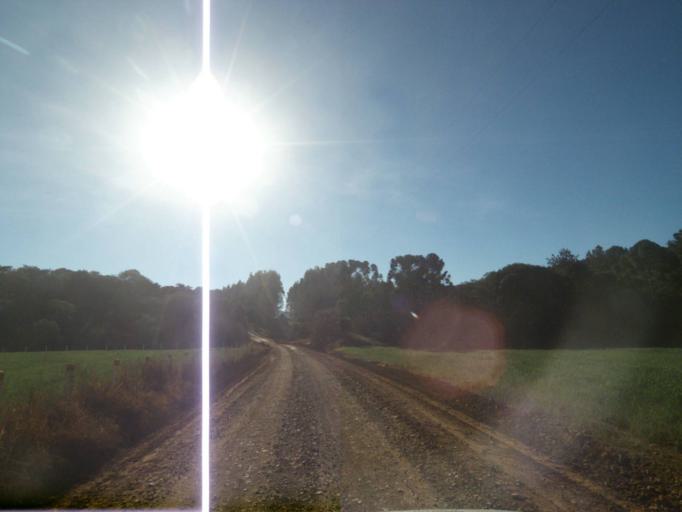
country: BR
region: Parana
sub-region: Tibagi
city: Tibagi
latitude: -24.5277
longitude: -50.4916
